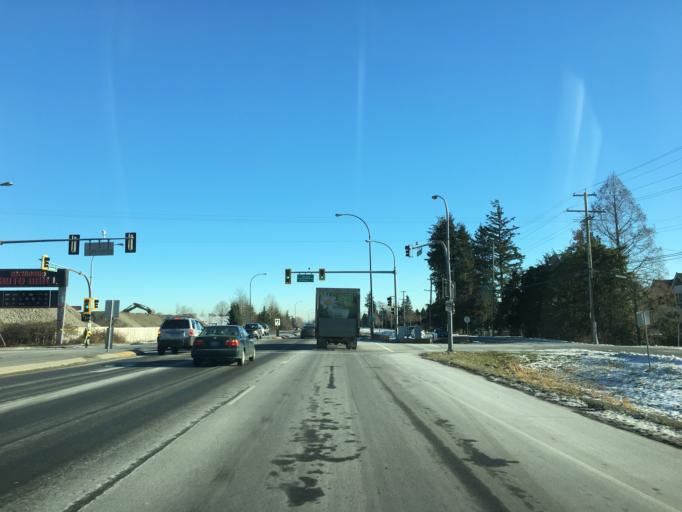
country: CA
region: British Columbia
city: Richmond
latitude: 49.1702
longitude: -123.0810
